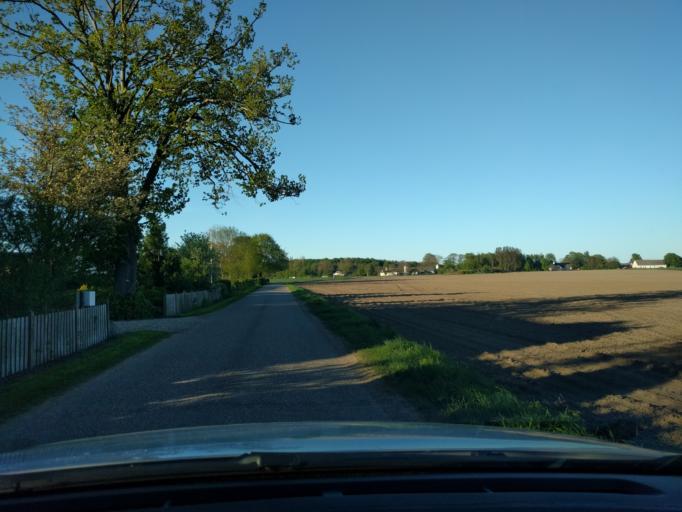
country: DK
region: South Denmark
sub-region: Nyborg Kommune
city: Ullerslev
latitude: 55.4048
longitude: 10.6545
